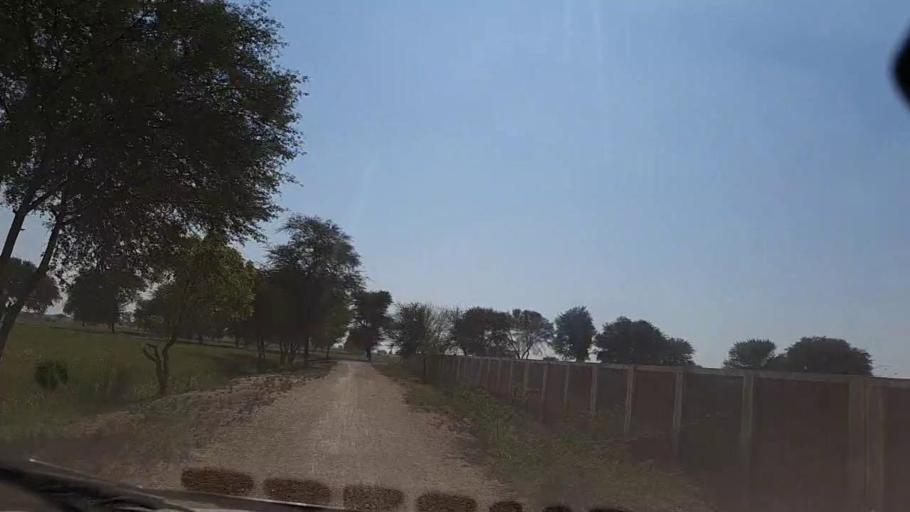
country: PK
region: Sindh
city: Mirpur Khas
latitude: 25.4352
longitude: 69.0479
